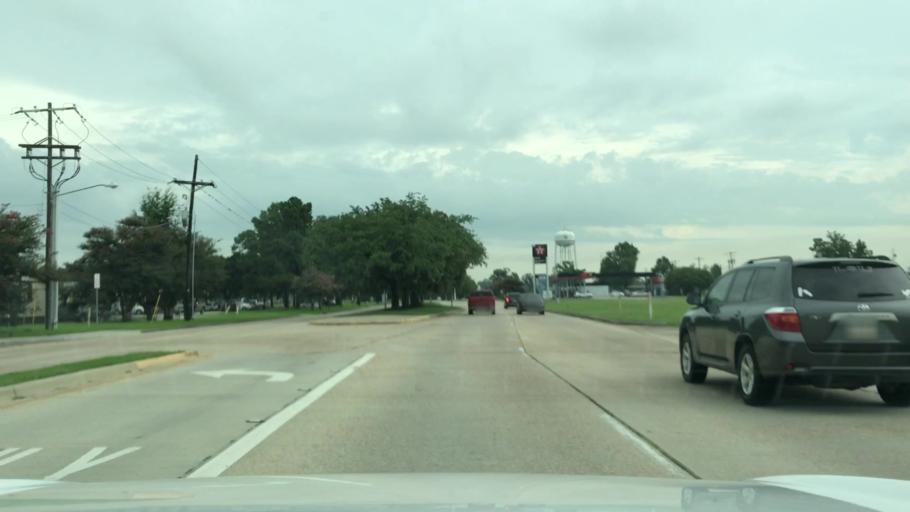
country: US
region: Louisiana
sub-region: East Baton Rouge Parish
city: Brownsfield
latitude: 30.5237
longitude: -91.1610
